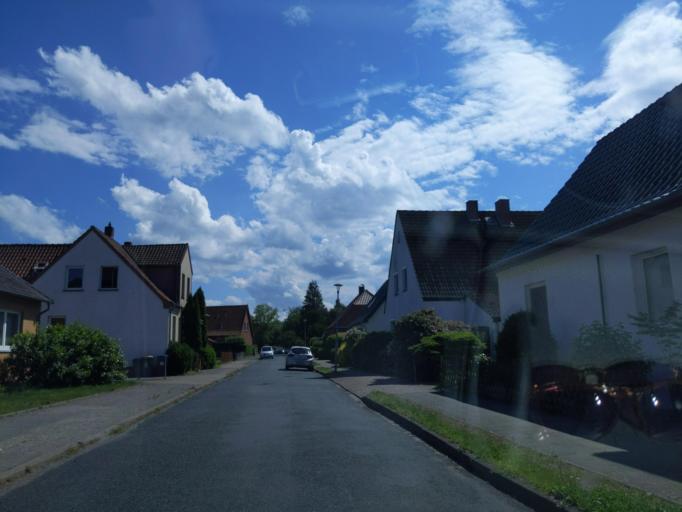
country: DE
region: Lower Saxony
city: Walsrode
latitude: 52.8622
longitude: 9.6036
